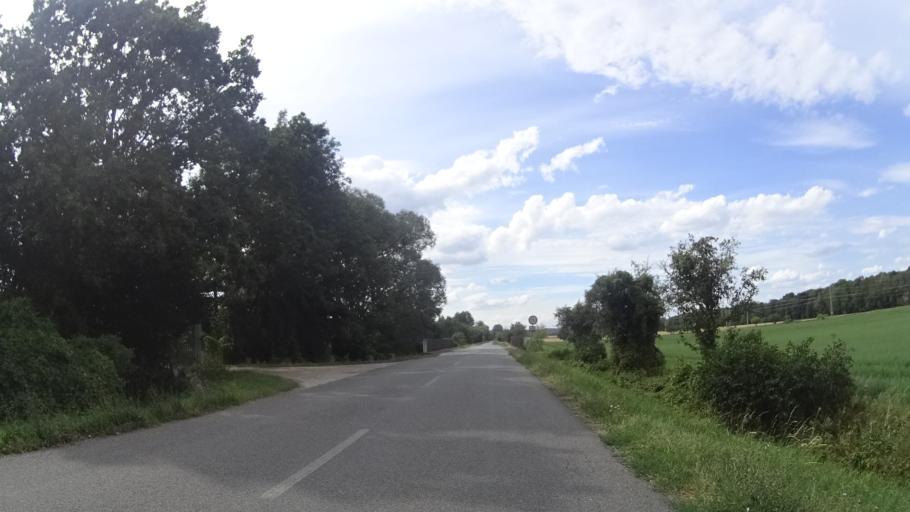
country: CZ
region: Olomoucky
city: Cervenka
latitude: 49.7124
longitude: 17.0609
